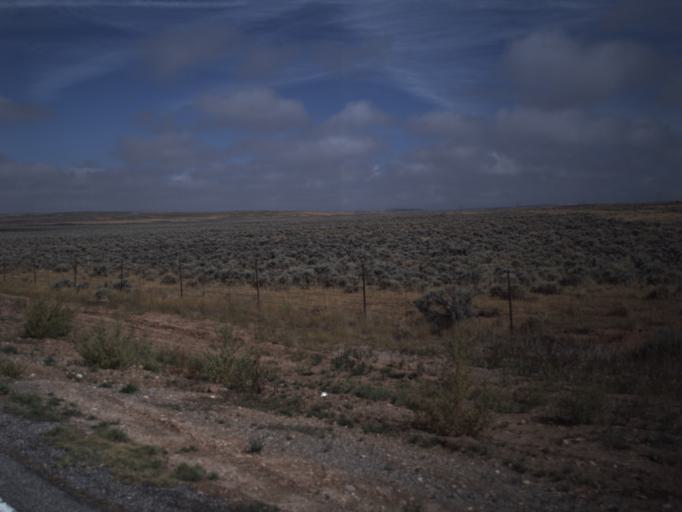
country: US
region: Wyoming
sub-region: Uinta County
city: Evanston
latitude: 41.4295
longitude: -111.0589
